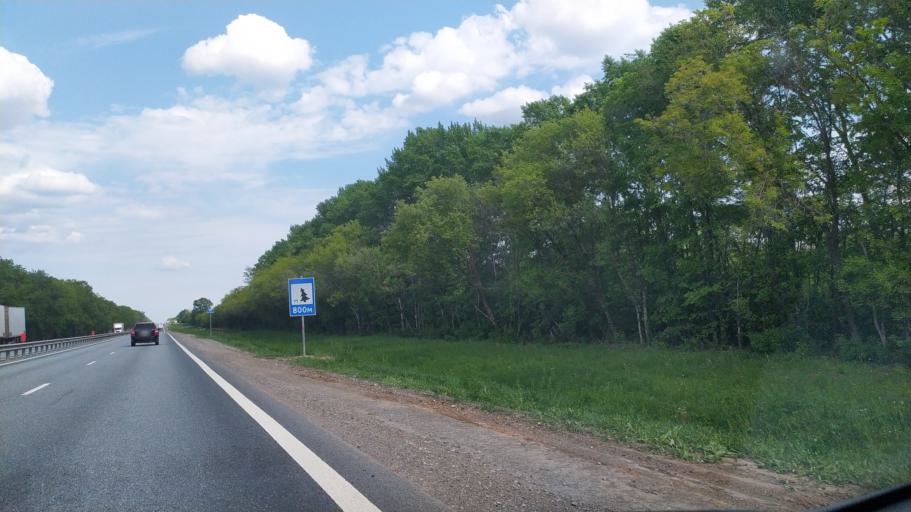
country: RU
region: Chuvashia
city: Yantikovo
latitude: 55.7909
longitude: 47.7713
